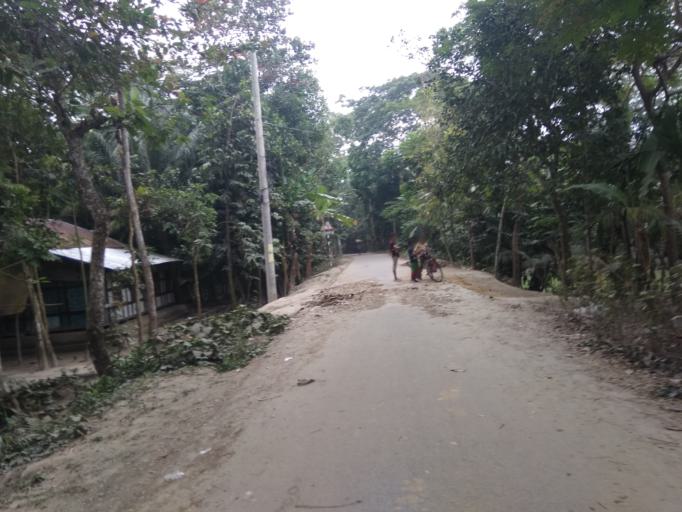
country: BD
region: Barisal
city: Mehendiganj
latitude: 22.9206
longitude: 90.3914
